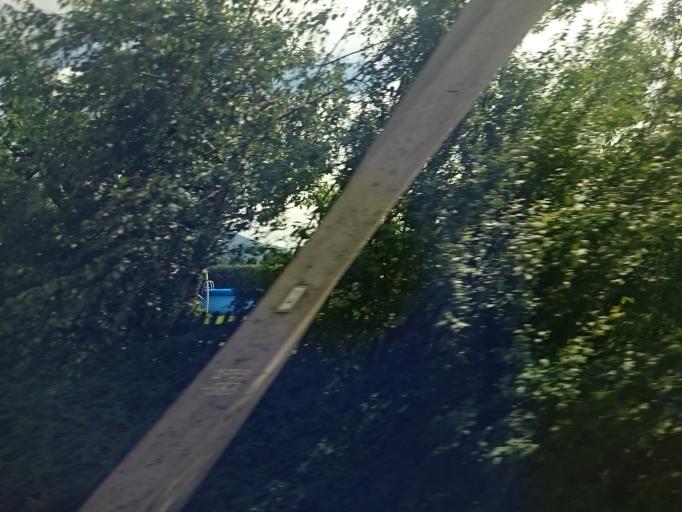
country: AT
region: Tyrol
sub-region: Politischer Bezirk Kufstein
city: Angath
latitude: 47.4974
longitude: 12.0708
